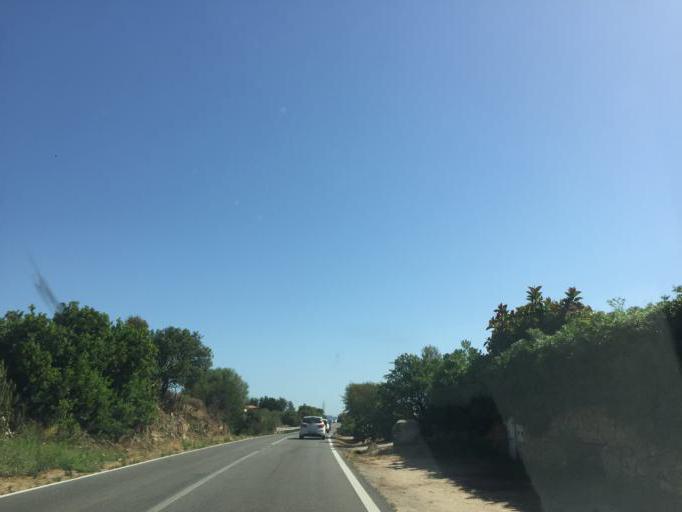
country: IT
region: Sardinia
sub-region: Provincia di Olbia-Tempio
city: San Teodoro
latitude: 40.7524
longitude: 9.6480
